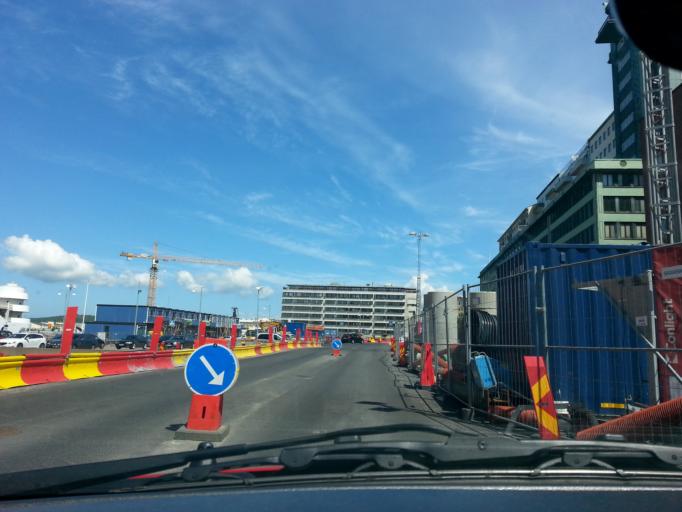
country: SE
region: Vaestra Goetaland
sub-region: Goteborg
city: Goeteborg
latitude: 57.7036
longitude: 11.9558
